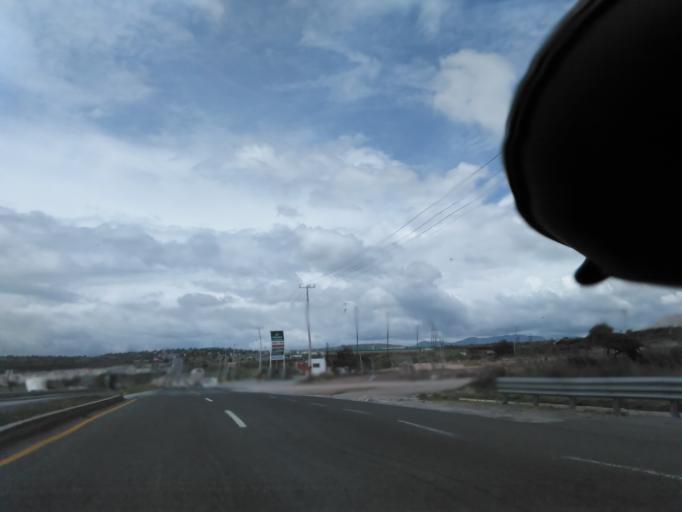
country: MX
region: Hidalgo
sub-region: Atotonilco de Tula
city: Paseos de la Pradera
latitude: 19.9125
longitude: -99.2396
